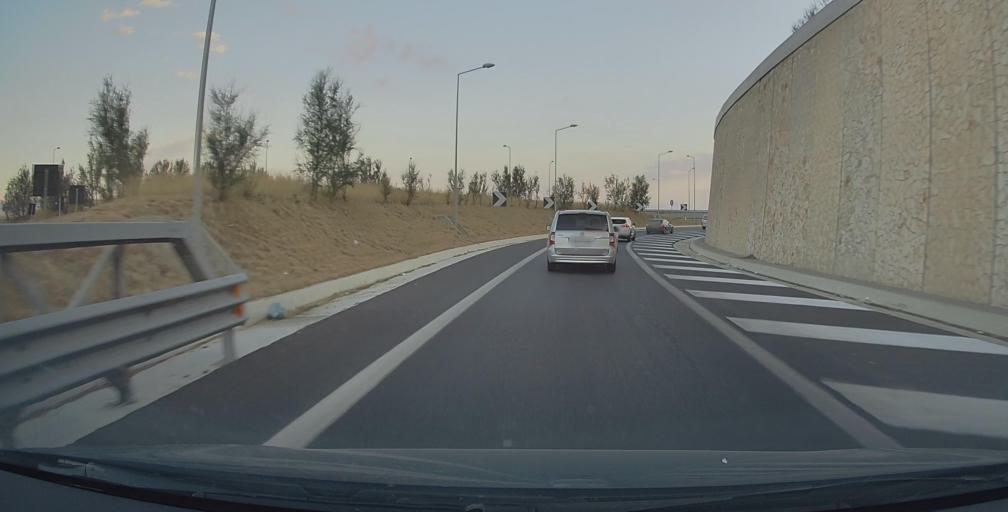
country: IT
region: Calabria
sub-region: Provincia di Reggio Calabria
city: Campo Calabro
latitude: 38.2058
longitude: 15.6419
